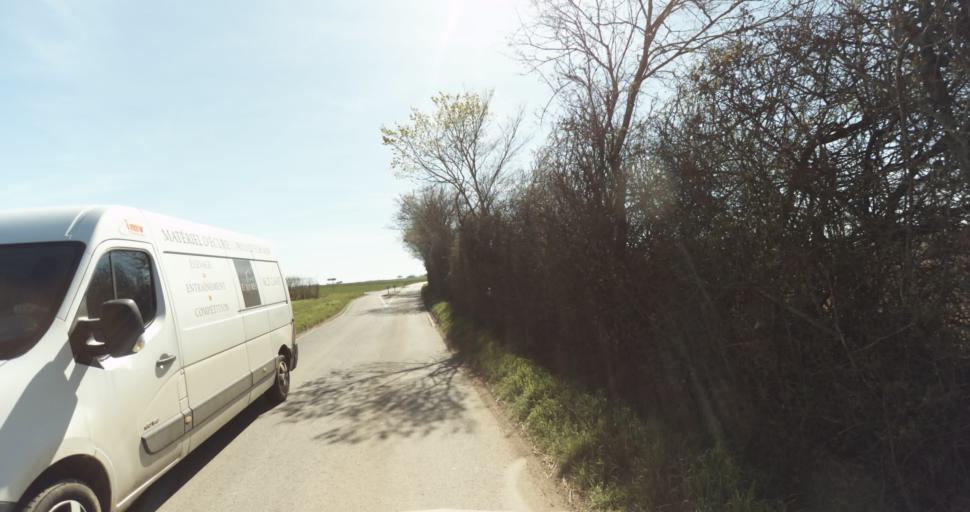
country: FR
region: Lower Normandy
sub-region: Departement du Calvados
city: Canon
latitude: 49.0506
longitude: -0.0647
